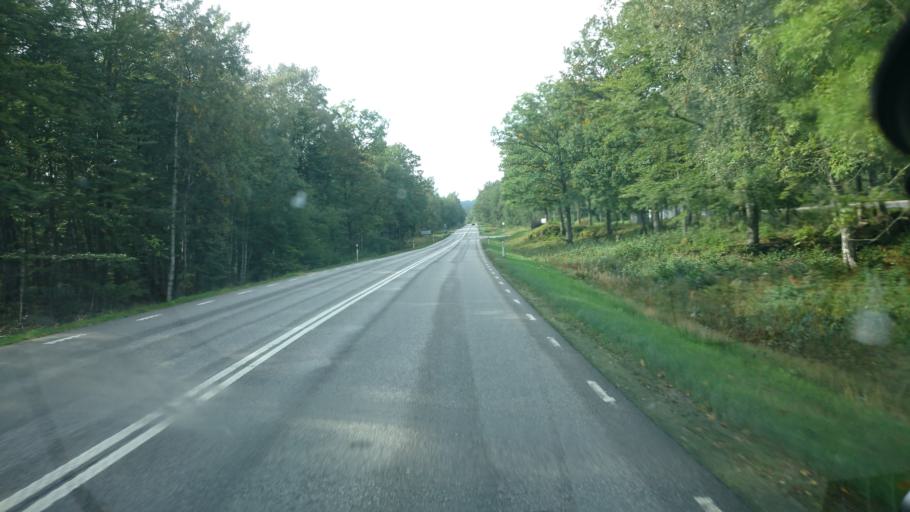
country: SE
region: Vaestra Goetaland
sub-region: Alingsas Kommun
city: Sollebrunn
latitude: 58.0656
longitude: 12.4768
